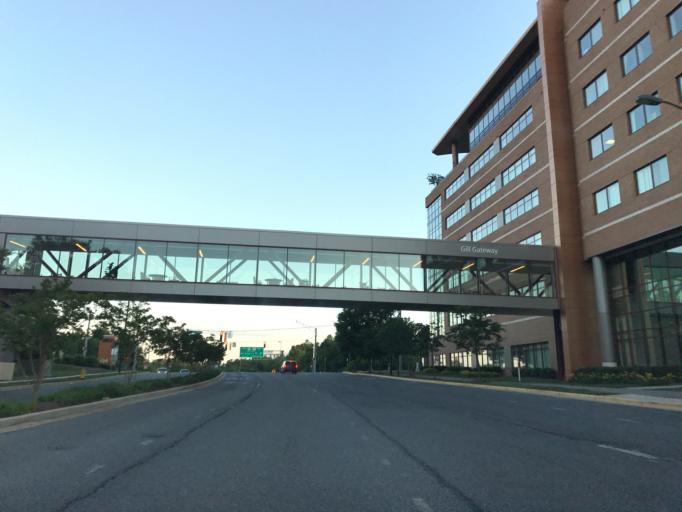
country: US
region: Maryland
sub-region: Anne Arundel County
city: Parole
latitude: 38.9899
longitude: -76.5364
